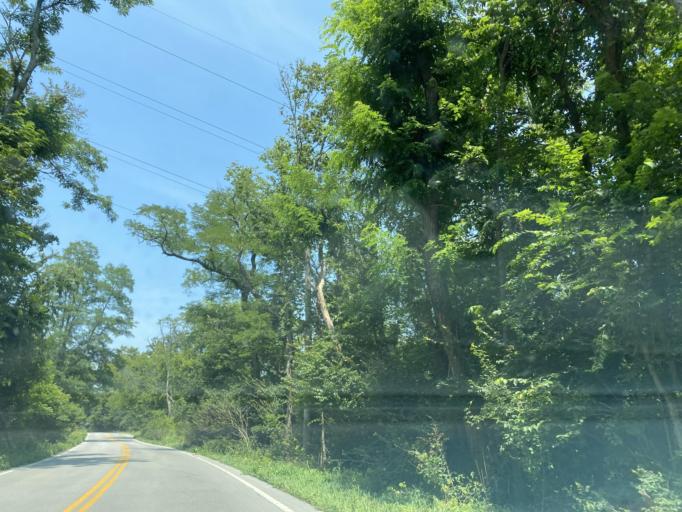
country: US
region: Kentucky
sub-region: Campbell County
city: Claryville
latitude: 38.9052
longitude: -84.4463
